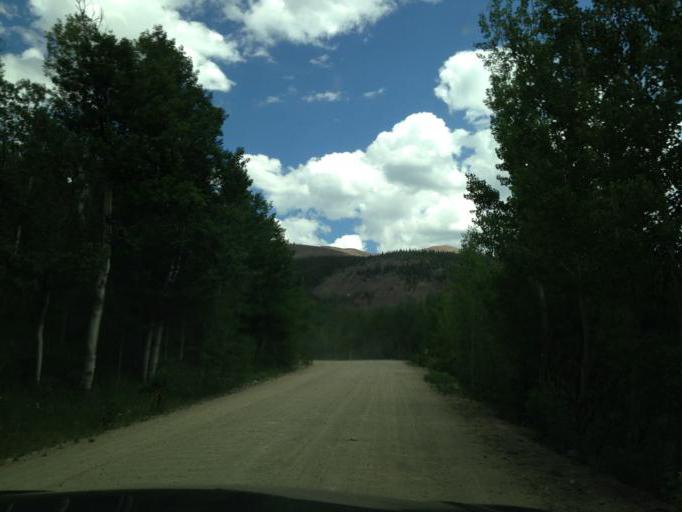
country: US
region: Colorado
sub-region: Park County
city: Fairplay
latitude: 39.3522
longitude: -105.9159
